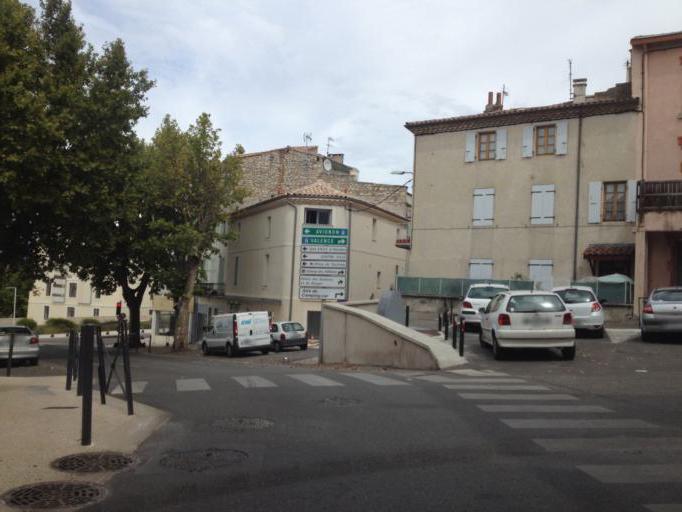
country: FR
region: Rhone-Alpes
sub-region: Departement de la Drome
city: Montelimar
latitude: 44.5607
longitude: 4.7532
